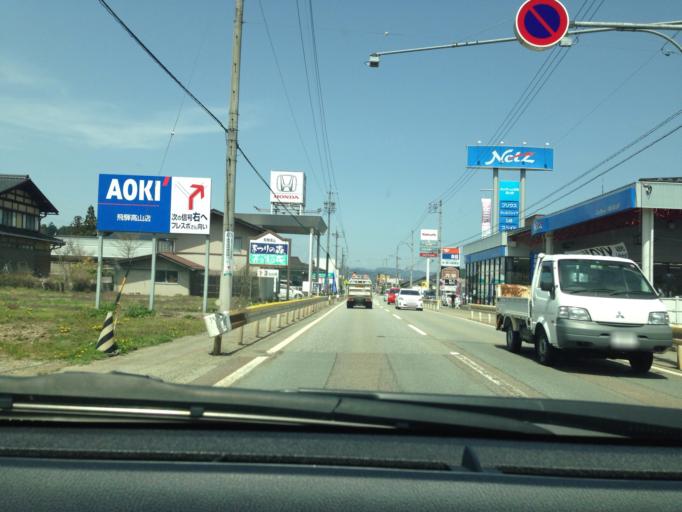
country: JP
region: Gifu
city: Takayama
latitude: 36.1179
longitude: 137.2631
